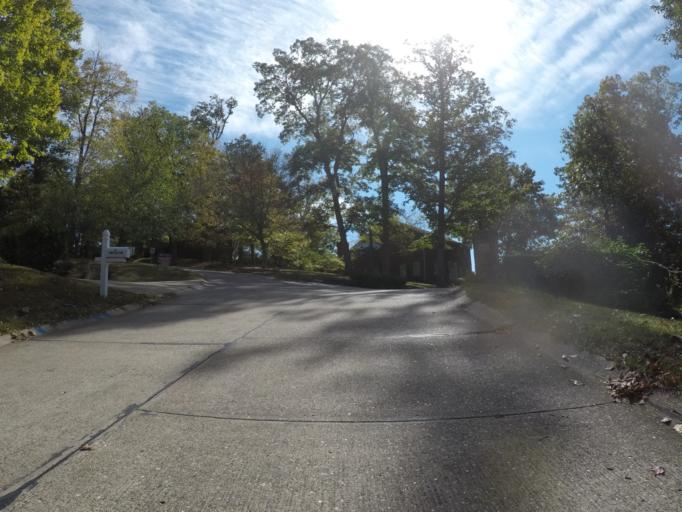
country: US
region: West Virginia
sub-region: Cabell County
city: Huntington
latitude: 38.3917
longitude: -82.3920
